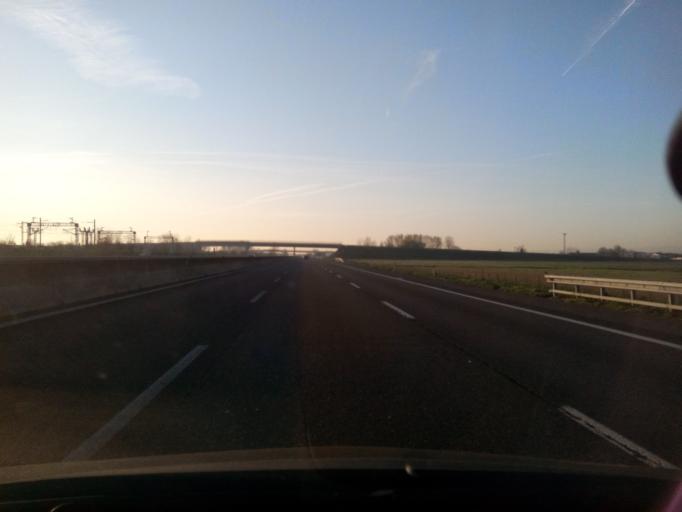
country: IT
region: Lombardy
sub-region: Provincia di Lodi
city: Livraga
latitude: 45.2012
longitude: 9.5483
